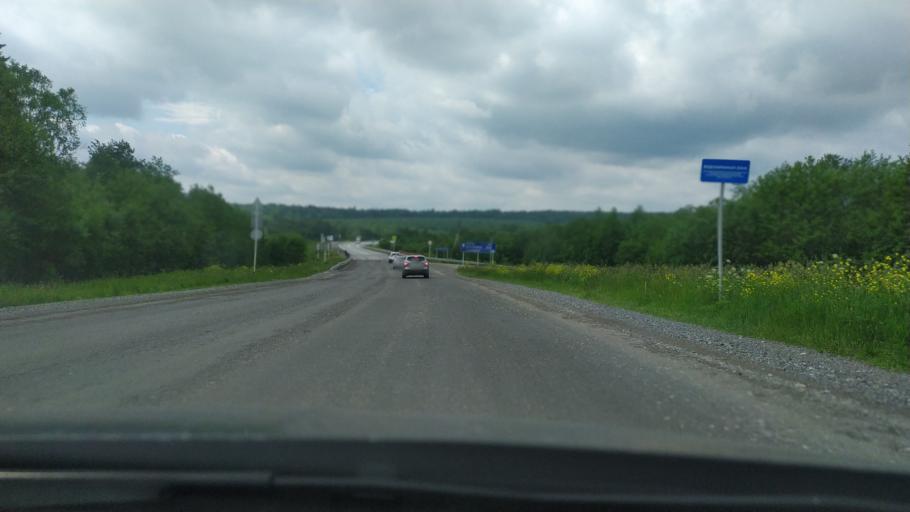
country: RU
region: Perm
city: Verkhnechusovskiye Gorodki
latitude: 58.2676
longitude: 57.3466
